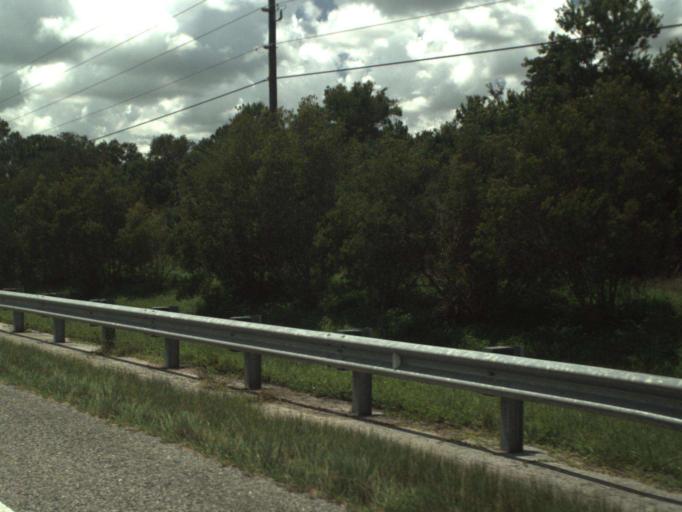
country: US
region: Florida
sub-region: Indian River County
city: Fellsmere
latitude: 27.6561
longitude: -80.7882
